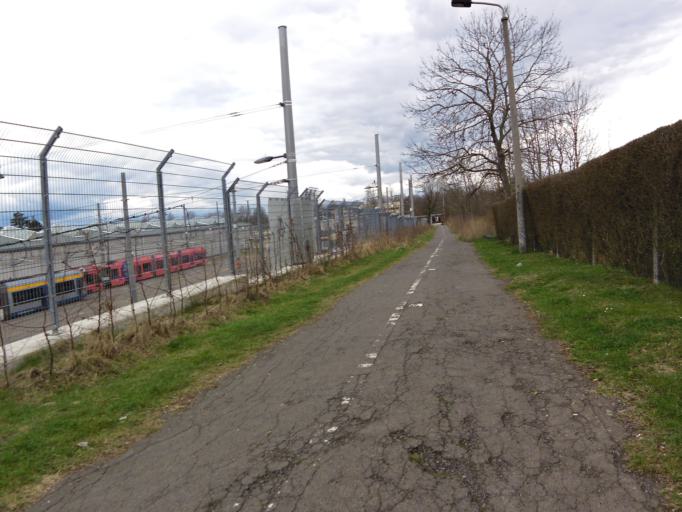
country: DE
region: Saxony
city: Markkleeberg
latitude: 51.2848
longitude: 12.3974
